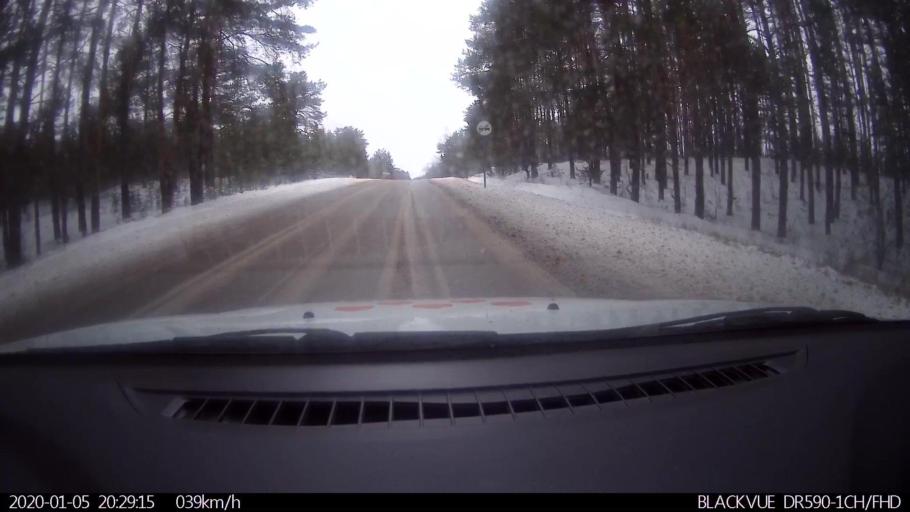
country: RU
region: Nizjnij Novgorod
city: Lukino
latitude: 56.3931
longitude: 43.7363
